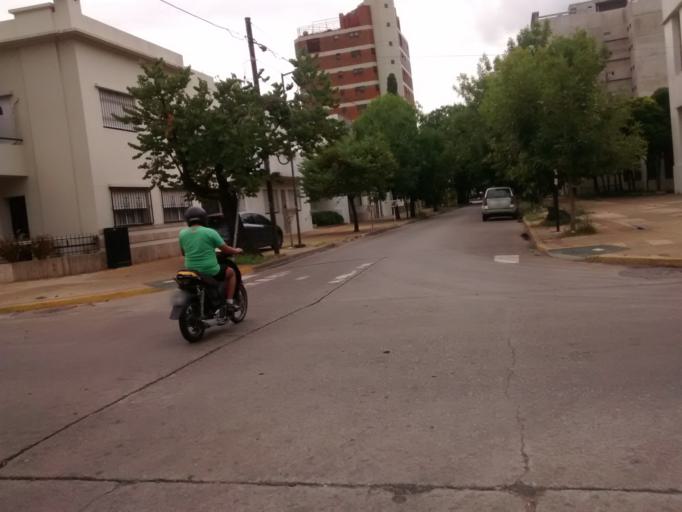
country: AR
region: Buenos Aires
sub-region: Partido de La Plata
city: La Plata
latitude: -34.9066
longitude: -57.9632
